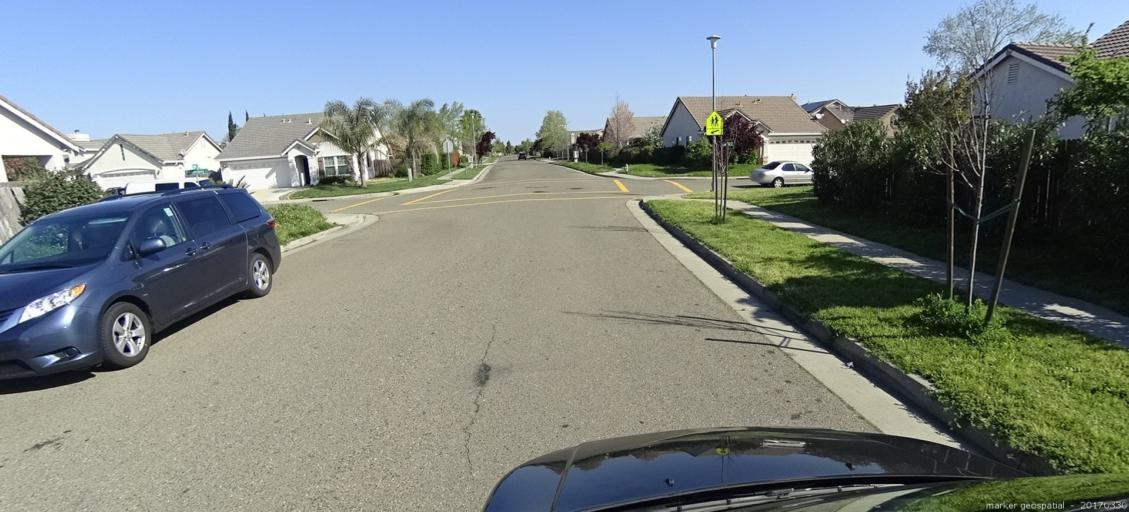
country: US
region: California
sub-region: Sacramento County
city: Laguna
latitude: 38.4453
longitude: -121.4101
